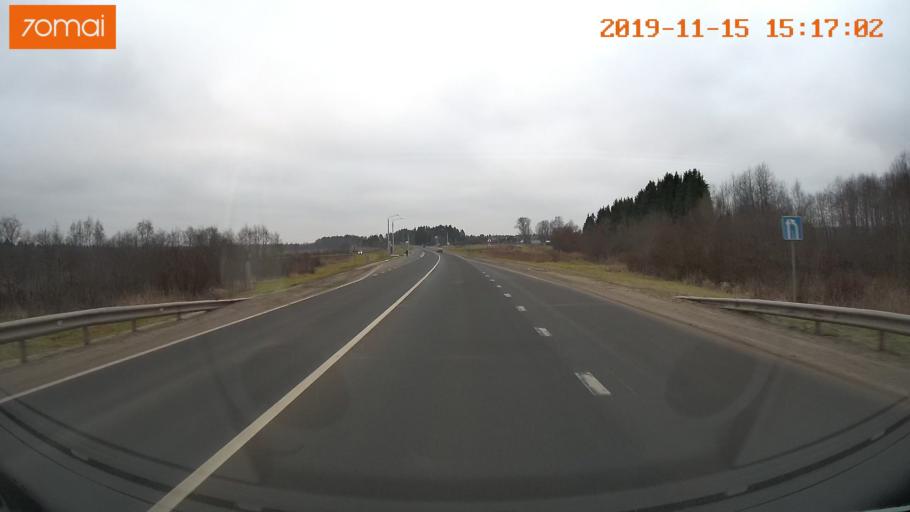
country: RU
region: Jaroslavl
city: Danilov
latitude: 58.2668
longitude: 40.1850
